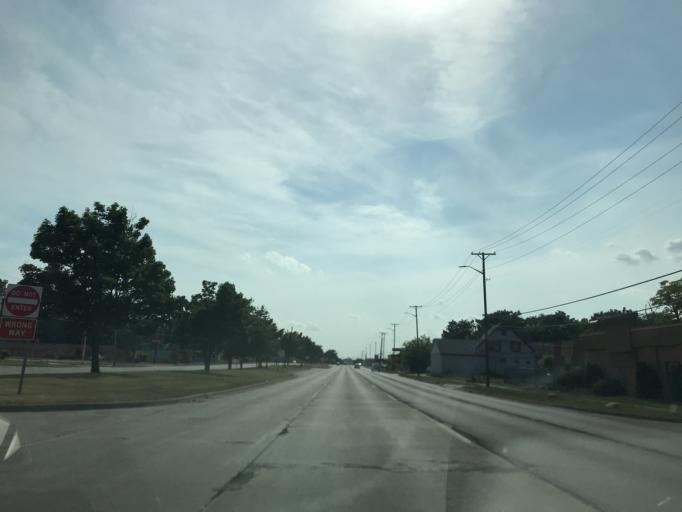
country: US
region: Michigan
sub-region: Wayne County
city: Inkster
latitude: 42.2967
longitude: -83.2932
